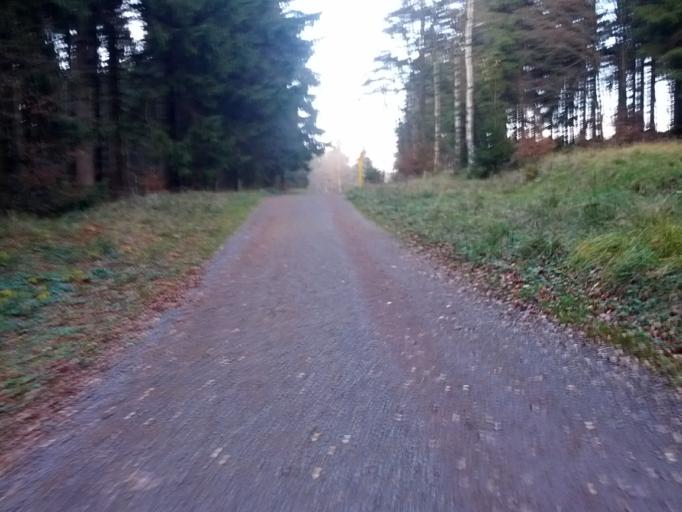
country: DE
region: Thuringia
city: Seebach
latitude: 50.8735
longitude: 10.4112
